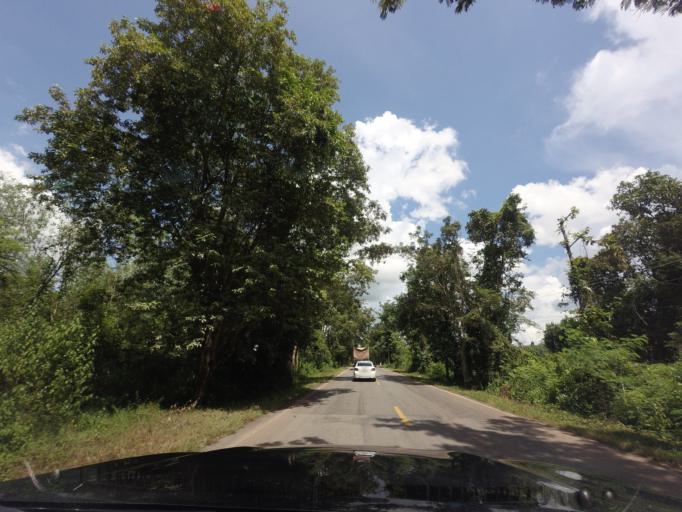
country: TH
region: Changwat Udon Thani
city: Phibun Rak
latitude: 17.5863
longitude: 103.0443
